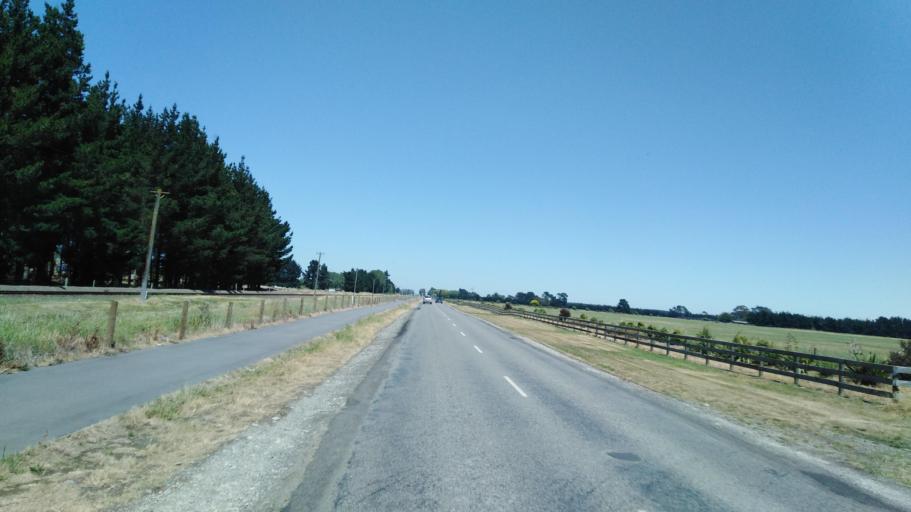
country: NZ
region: Canterbury
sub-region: Selwyn District
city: Prebbleton
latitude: -43.5615
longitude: 172.4546
